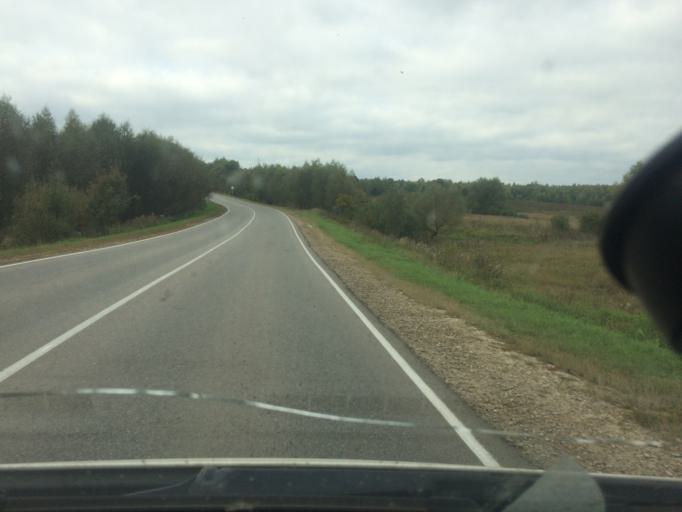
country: RU
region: Tula
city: Odoyev
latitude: 53.9997
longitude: 36.6670
